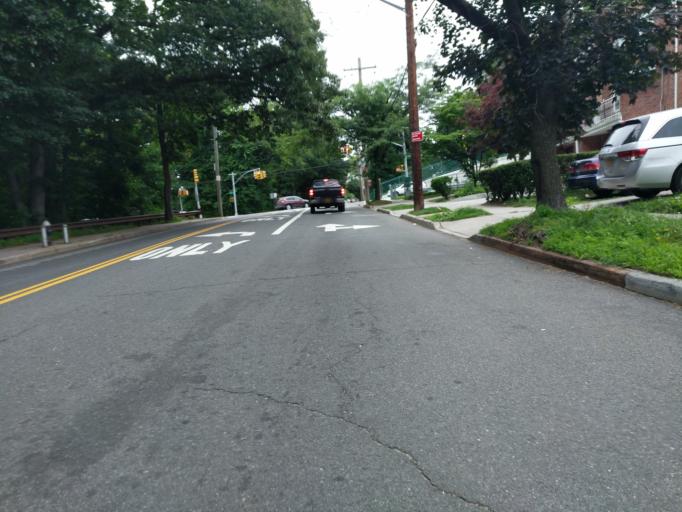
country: US
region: New York
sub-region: Queens County
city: Jamaica
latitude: 40.7421
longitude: -73.8053
